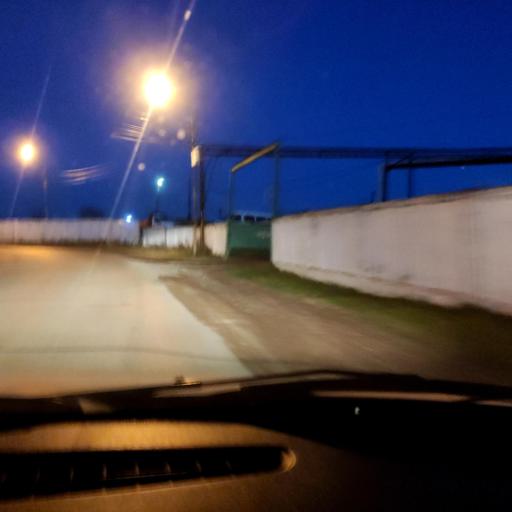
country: RU
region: Bashkortostan
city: Ufa
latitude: 54.8505
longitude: 56.0841
